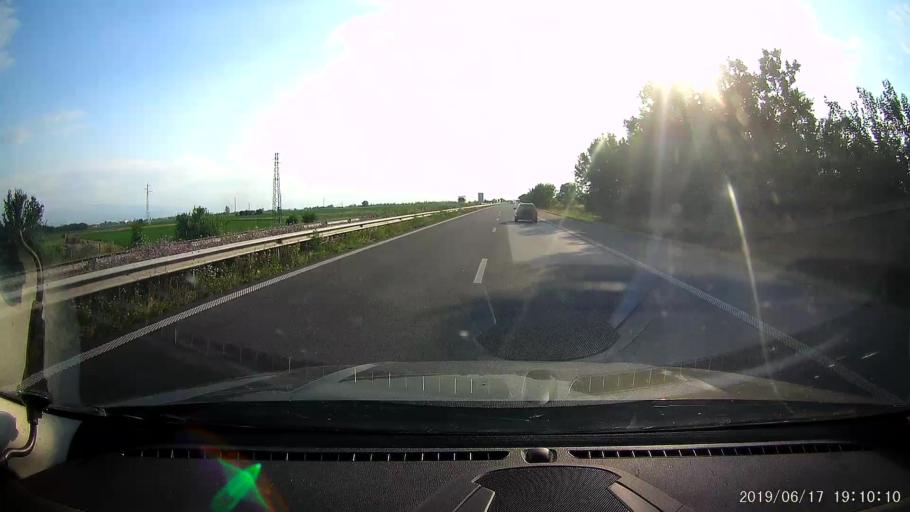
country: BG
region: Plovdiv
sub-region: Obshtina Plovdiv
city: Plovdiv
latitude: 42.2109
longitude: 24.7985
